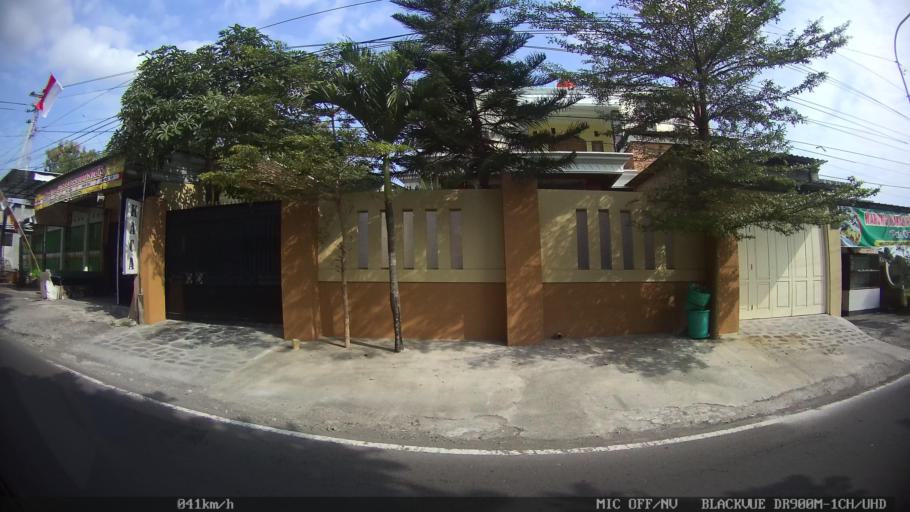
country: ID
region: Daerah Istimewa Yogyakarta
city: Depok
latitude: -7.7225
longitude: 110.4378
